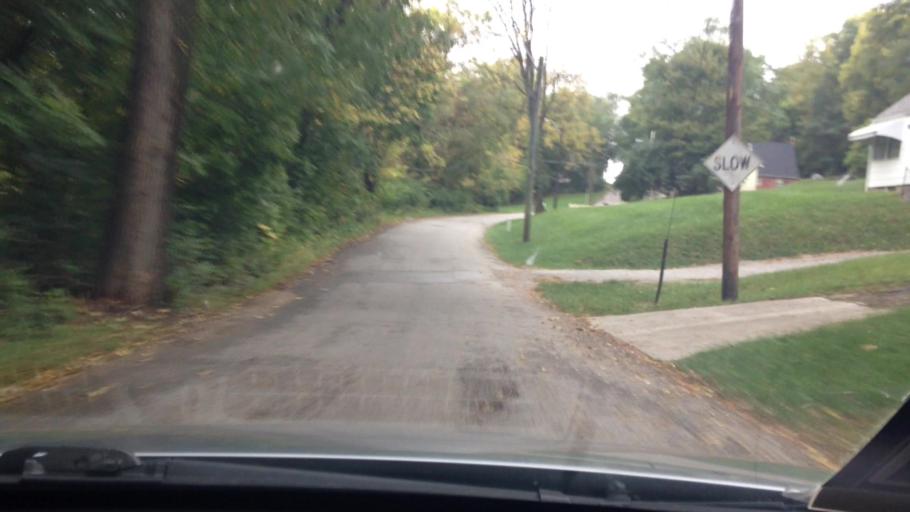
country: US
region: Missouri
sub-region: Clay County
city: North Kansas City
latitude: 39.1610
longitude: -94.5479
